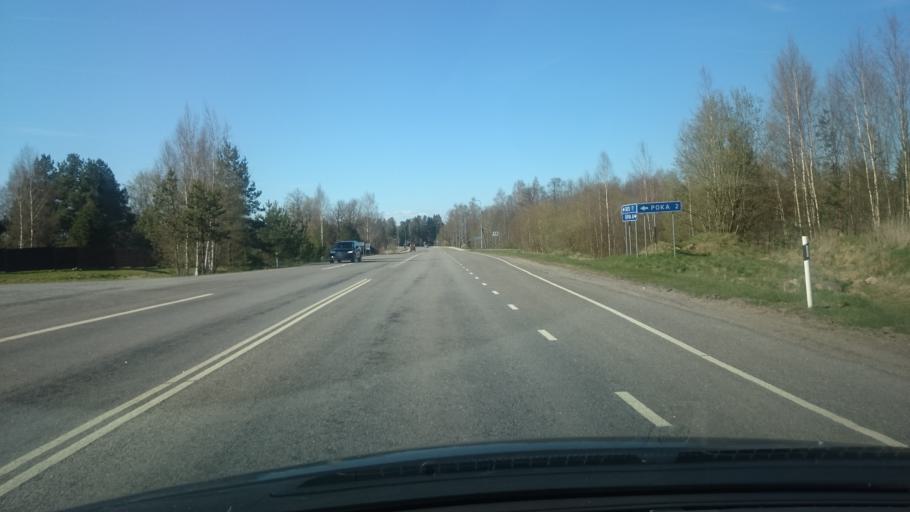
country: EE
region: Tartu
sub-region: UElenurme vald
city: Ulenurme
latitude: 58.3287
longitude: 26.9798
